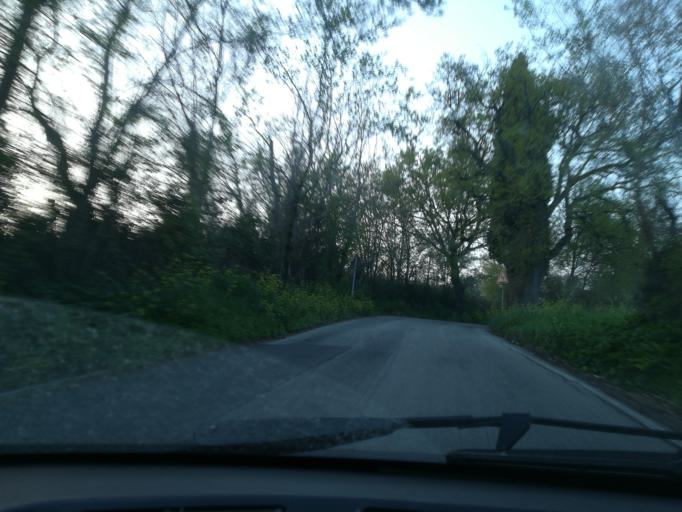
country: IT
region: The Marches
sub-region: Provincia di Macerata
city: Macerata
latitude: 43.2785
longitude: 13.4490
